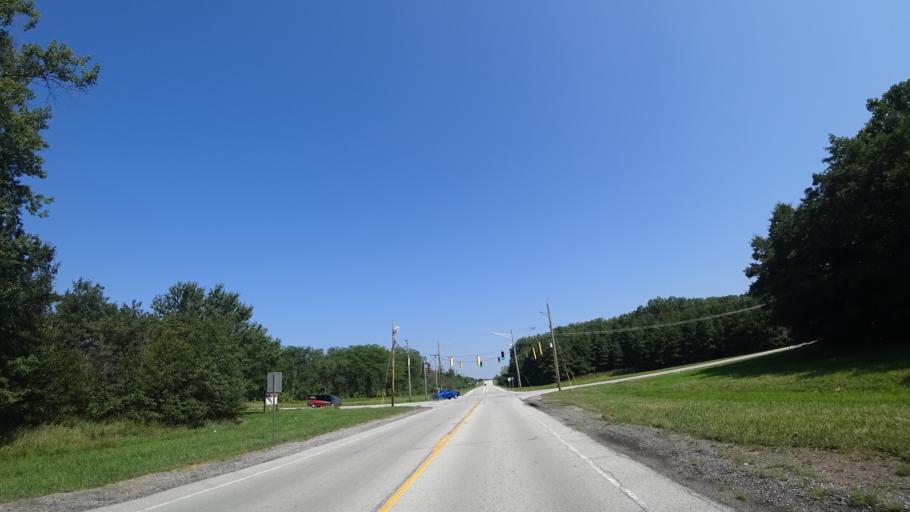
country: US
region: Illinois
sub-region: Cook County
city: Country Club Hills
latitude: 41.5564
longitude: -87.7524
